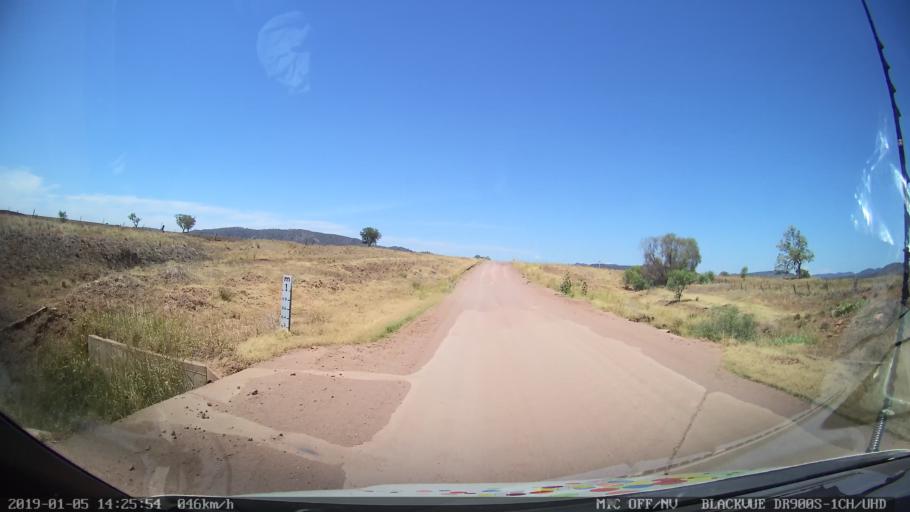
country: AU
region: New South Wales
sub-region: Liverpool Plains
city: Quirindi
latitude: -31.2408
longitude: 150.5503
